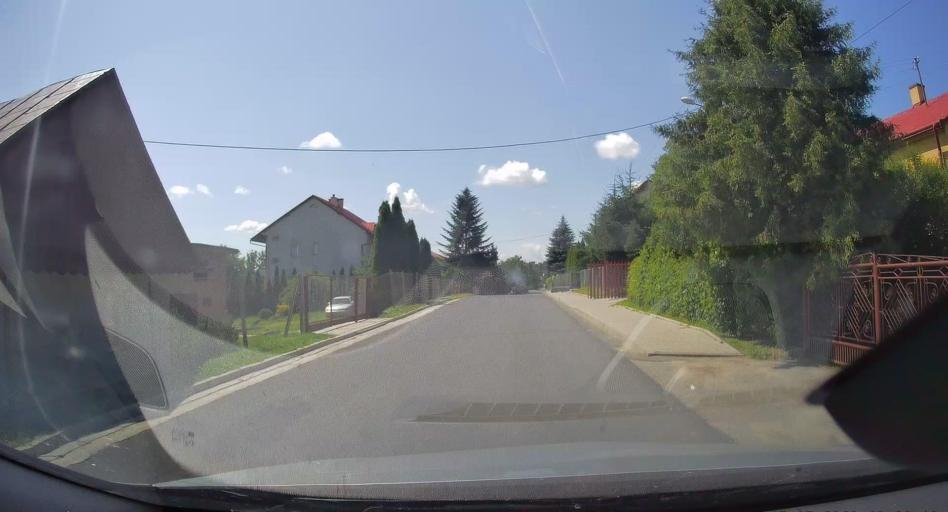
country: PL
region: Subcarpathian Voivodeship
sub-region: Powiat przemyski
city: Medyka
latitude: 49.8444
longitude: 22.8868
